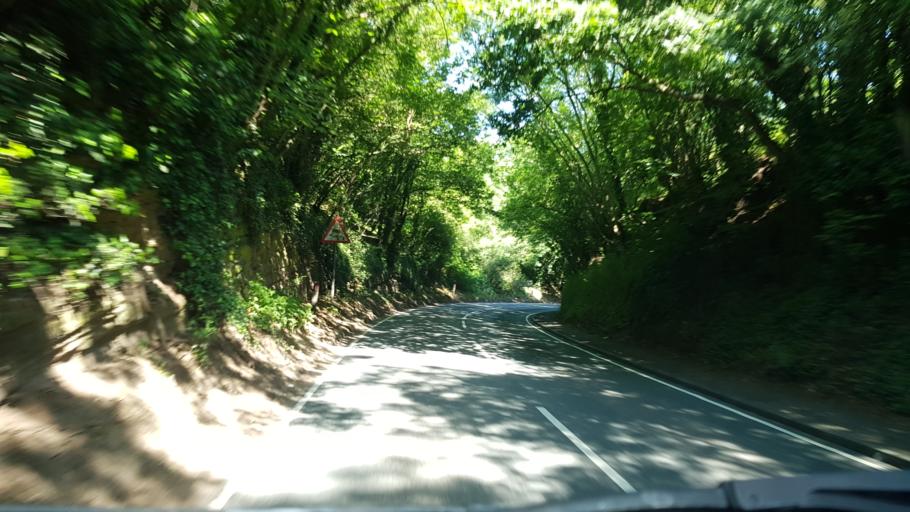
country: GB
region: England
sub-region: Worcestershire
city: Bewdley
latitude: 52.3612
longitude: -2.3019
